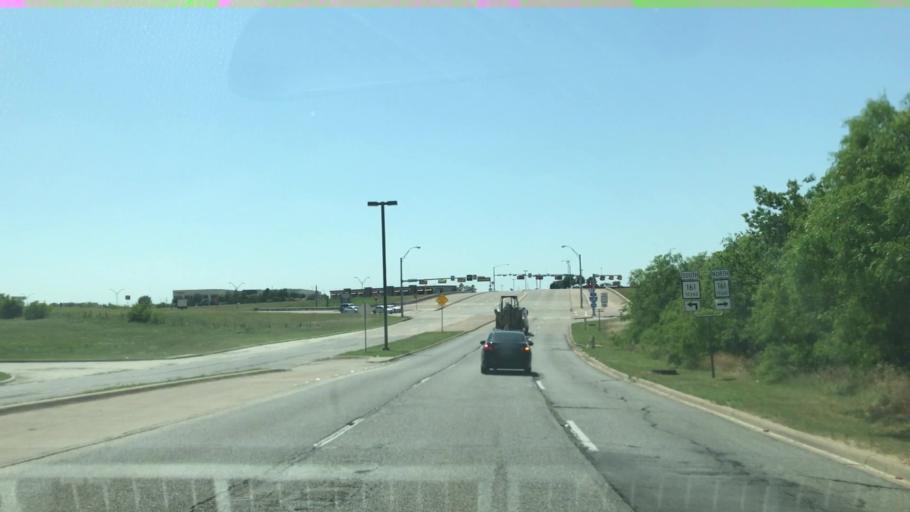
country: US
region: Texas
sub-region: Dallas County
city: Irving
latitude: 32.8655
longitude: -97.0003
